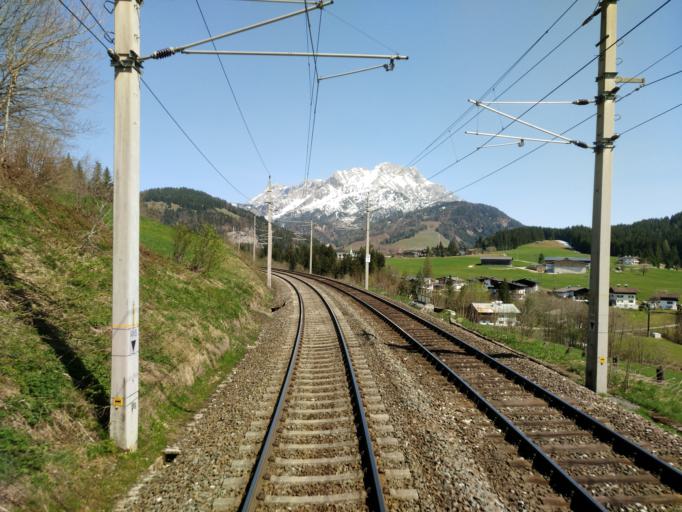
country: AT
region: Tyrol
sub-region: Politischer Bezirk Kitzbuhel
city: Hochfilzen
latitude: 47.4676
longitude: 12.6013
